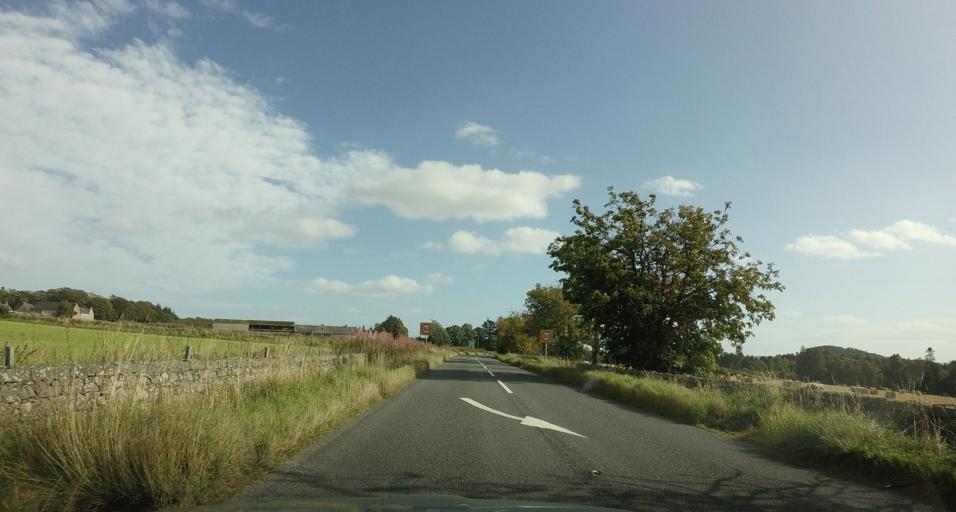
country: GB
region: Scotland
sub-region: Aberdeenshire
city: Westhill
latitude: 57.1610
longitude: -2.3469
